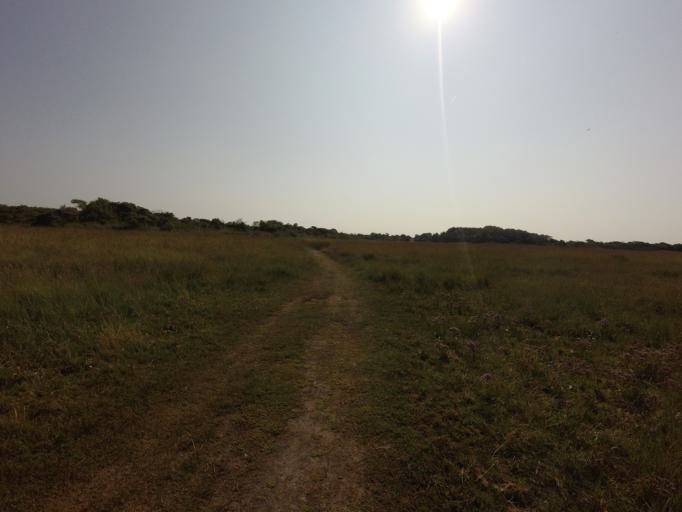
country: NL
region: Friesland
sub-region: Gemeente Schiermonnikoog
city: Schiermonnikoog
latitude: 53.4896
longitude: 6.2251
